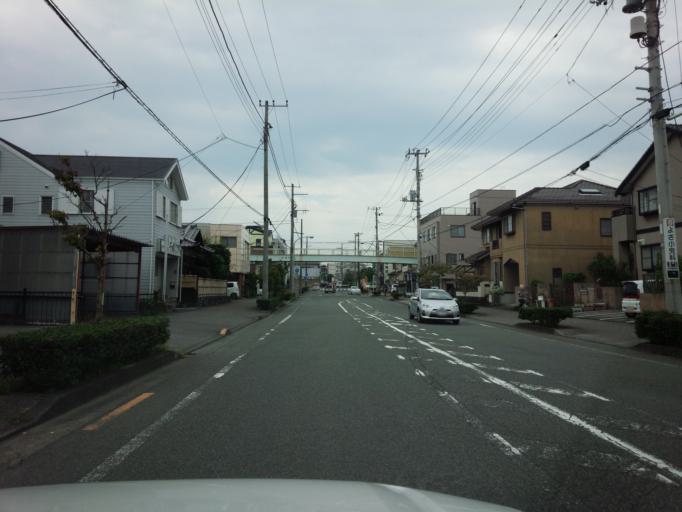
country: JP
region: Shizuoka
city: Numazu
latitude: 35.1262
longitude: 138.7996
